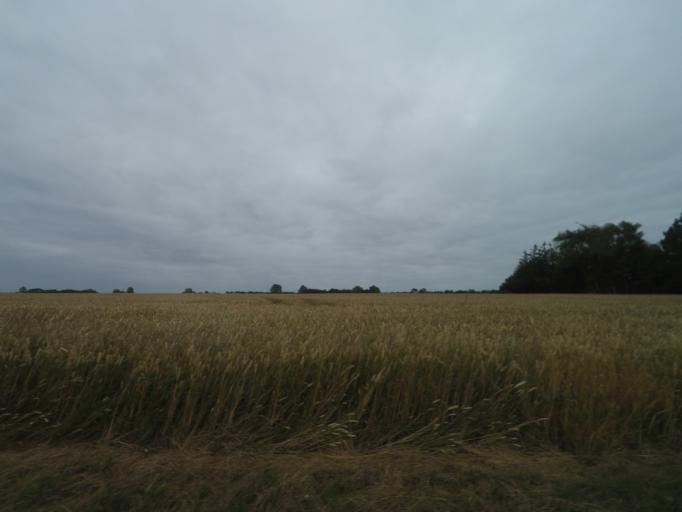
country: DK
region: South Denmark
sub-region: Nordfyns Kommune
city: Otterup
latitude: 55.5597
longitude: 10.4292
